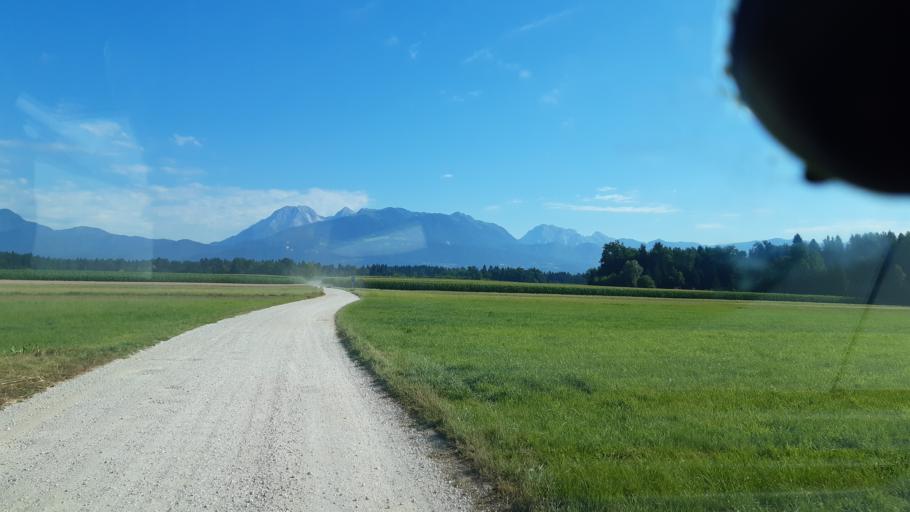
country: SI
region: Vodice
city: Vodice
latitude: 46.1859
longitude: 14.5079
